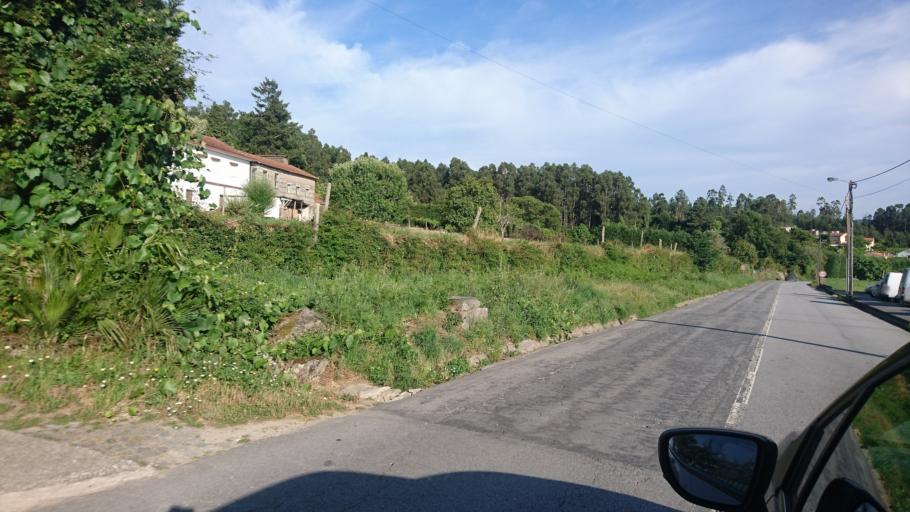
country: PT
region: Porto
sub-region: Paredes
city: Recarei
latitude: 41.1333
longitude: -8.3747
